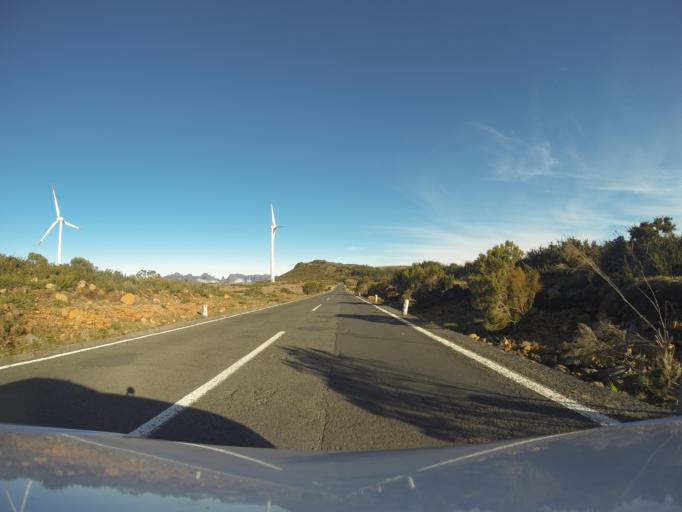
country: PT
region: Madeira
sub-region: Sao Vicente
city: Sao Vicente
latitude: 32.7588
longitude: -17.0619
